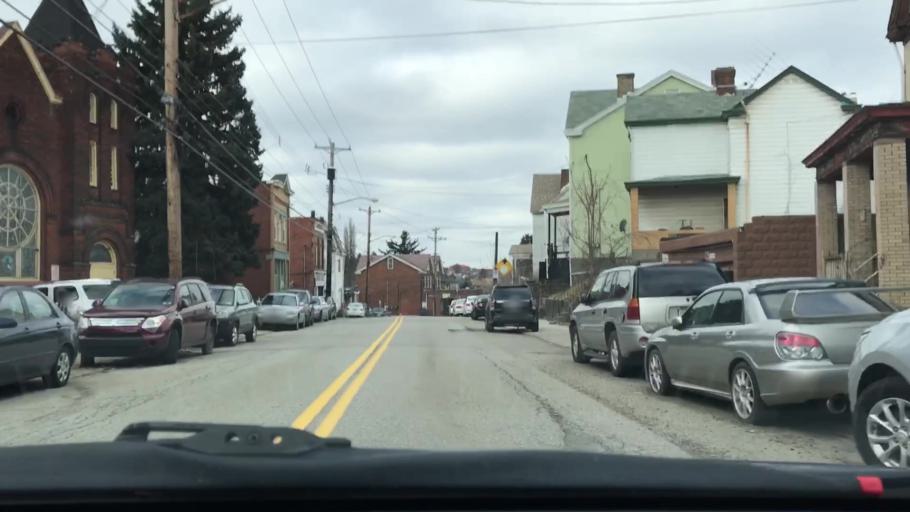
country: US
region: Pennsylvania
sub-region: Allegheny County
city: Mount Oliver
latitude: 40.4173
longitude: -79.9746
